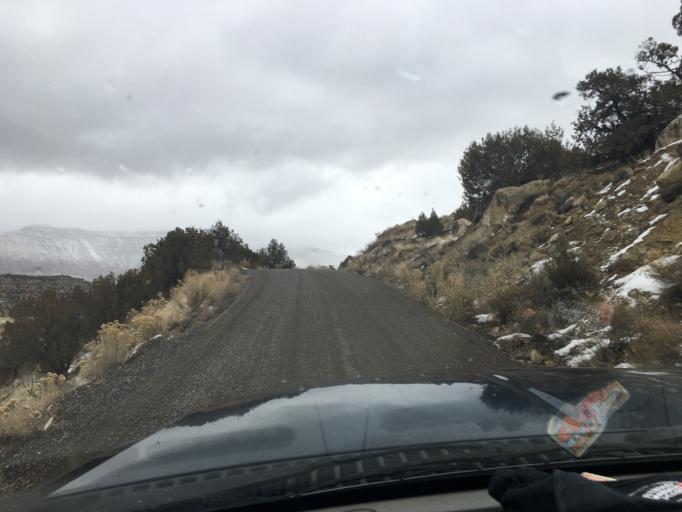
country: US
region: Colorado
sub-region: Garfield County
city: Parachute
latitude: 39.3486
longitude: -108.1741
